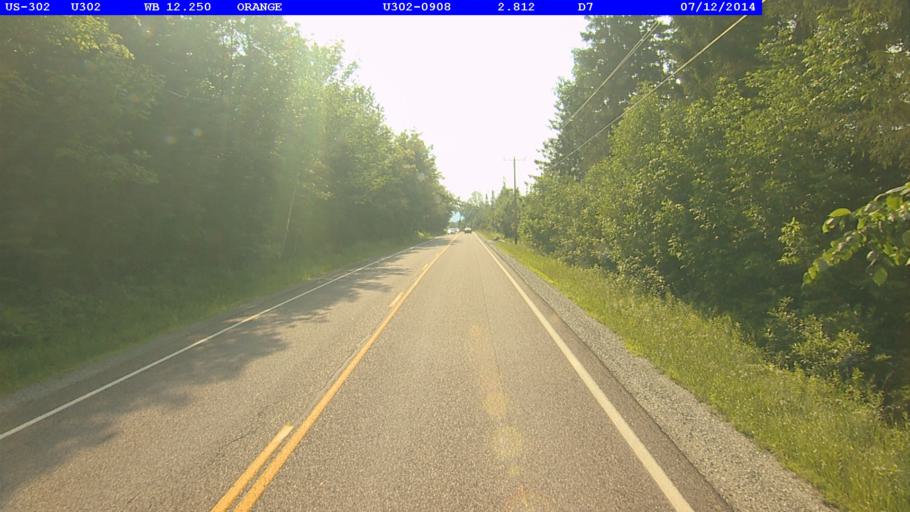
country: US
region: Vermont
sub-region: Washington County
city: South Barre
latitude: 44.1465
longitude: -72.3832
